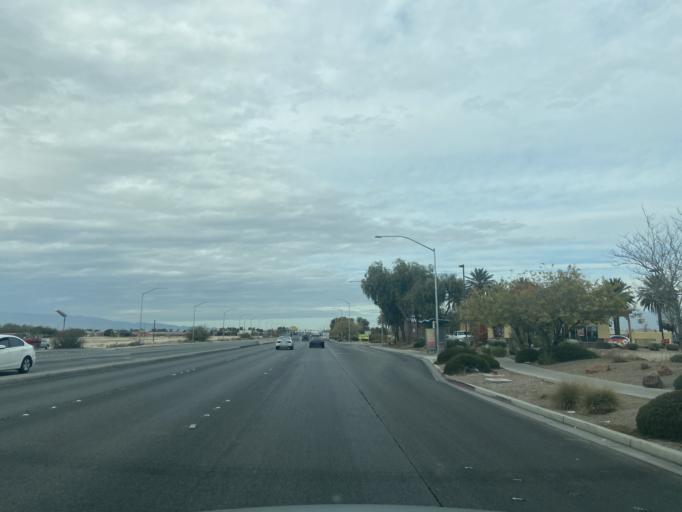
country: US
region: Nevada
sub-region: Clark County
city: Las Vegas
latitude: 36.2030
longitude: -115.1991
